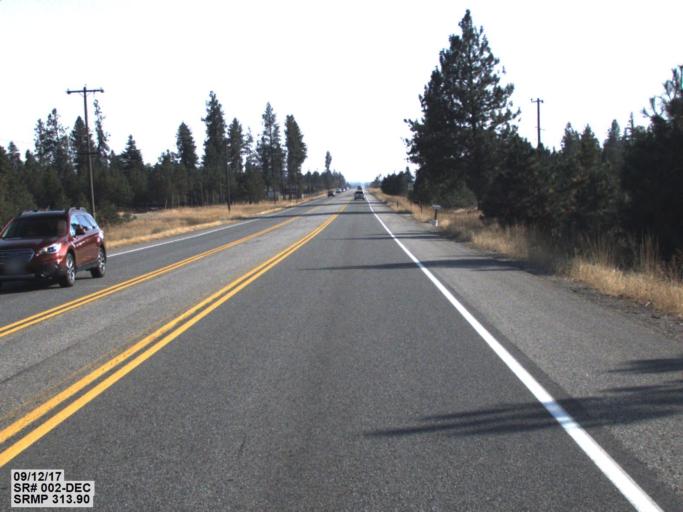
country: US
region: Washington
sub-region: Spokane County
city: Deer Park
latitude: 48.0246
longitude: -117.3497
